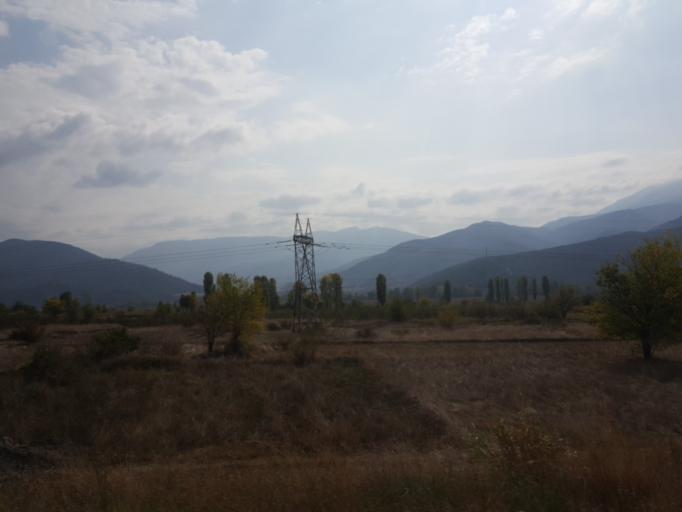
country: TR
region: Corum
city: Hacihamza
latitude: 41.1167
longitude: 34.4019
